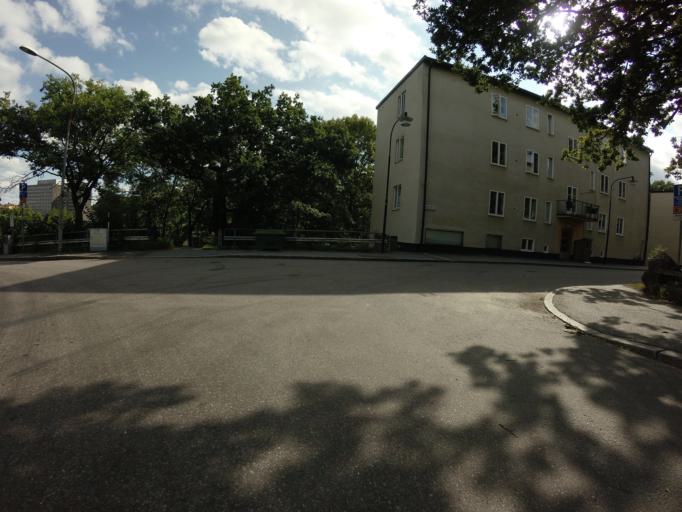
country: SE
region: Stockholm
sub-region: Stockholms Kommun
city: OEstermalm
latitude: 59.3524
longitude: 18.0964
